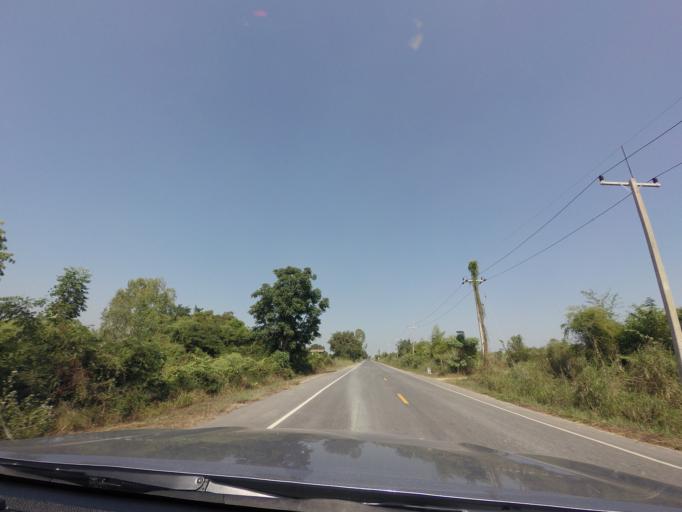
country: TH
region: Sukhothai
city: Sukhothai
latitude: 17.0769
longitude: 99.7907
